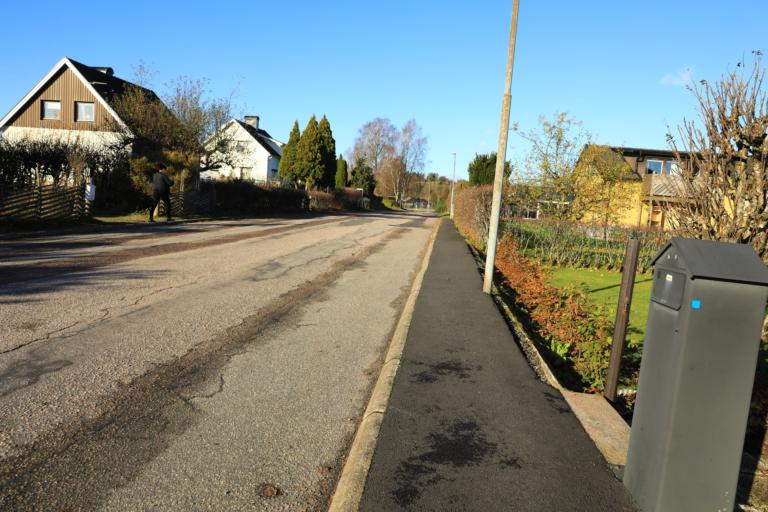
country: SE
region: Vaestra Goetaland
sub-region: Marks Kommun
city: Kinna
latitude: 57.5006
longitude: 12.6757
